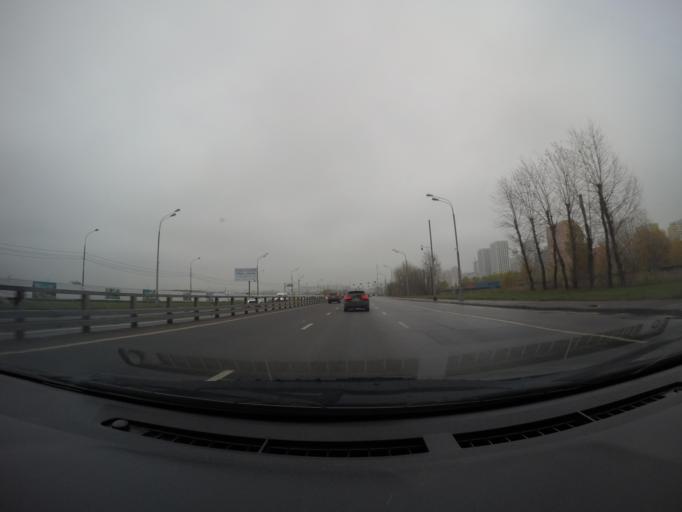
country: RU
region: Moskovskaya
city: Shcherbinka
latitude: 55.5199
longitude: 37.5774
